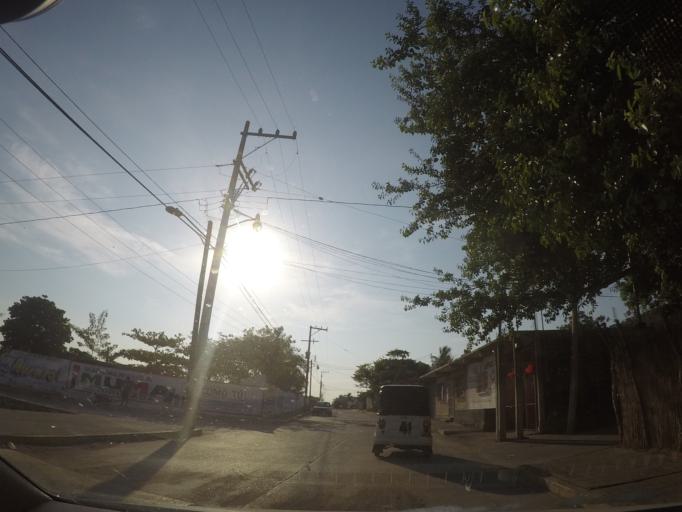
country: MX
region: Oaxaca
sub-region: Santo Domingo Tehuantepec
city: La Noria
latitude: 16.2464
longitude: -95.1489
